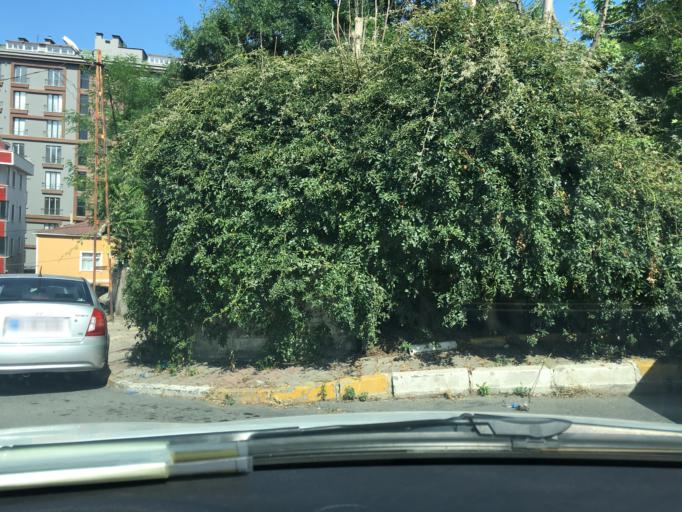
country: TR
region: Istanbul
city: Sisli
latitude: 41.0798
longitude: 28.9445
